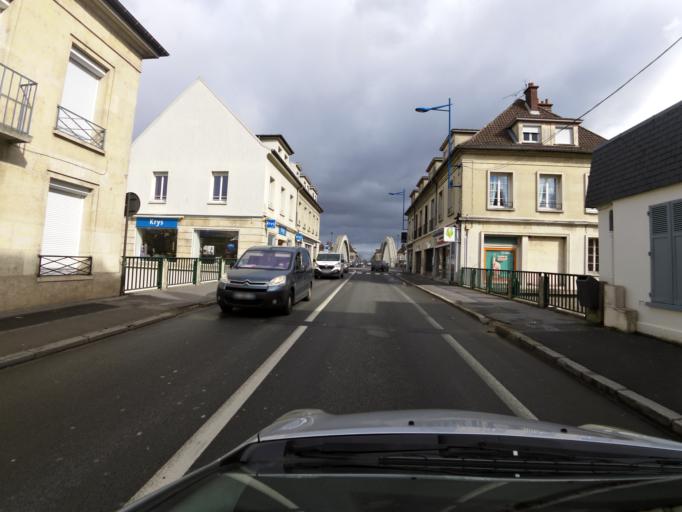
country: FR
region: Picardie
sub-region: Departement de l'Oise
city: Pont-Sainte-Maxence
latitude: 49.3019
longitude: 2.6044
